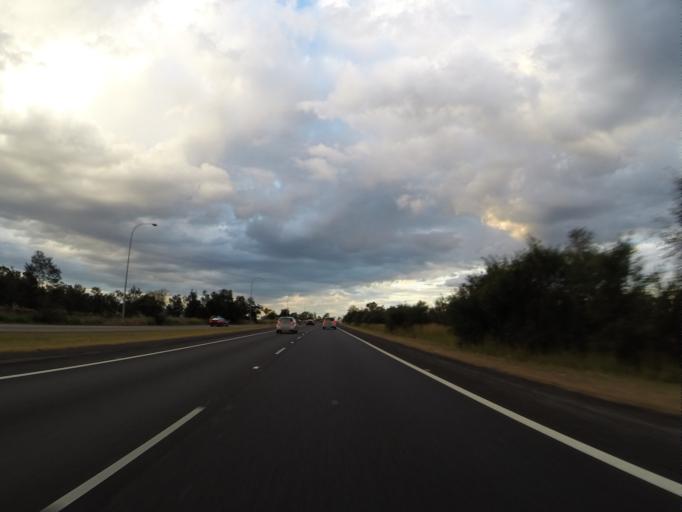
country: AU
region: New South Wales
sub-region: Wollondilly
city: Douglas Park
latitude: -34.2262
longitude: 150.6704
